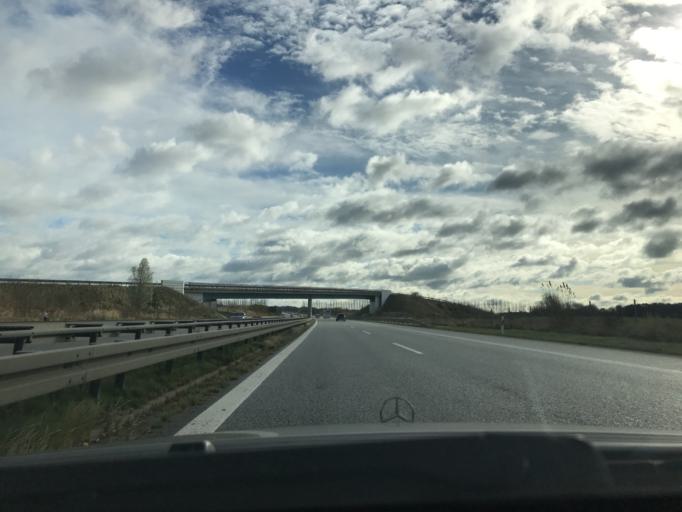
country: DE
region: Brandenburg
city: Schonfeld
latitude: 53.4562
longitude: 13.9717
